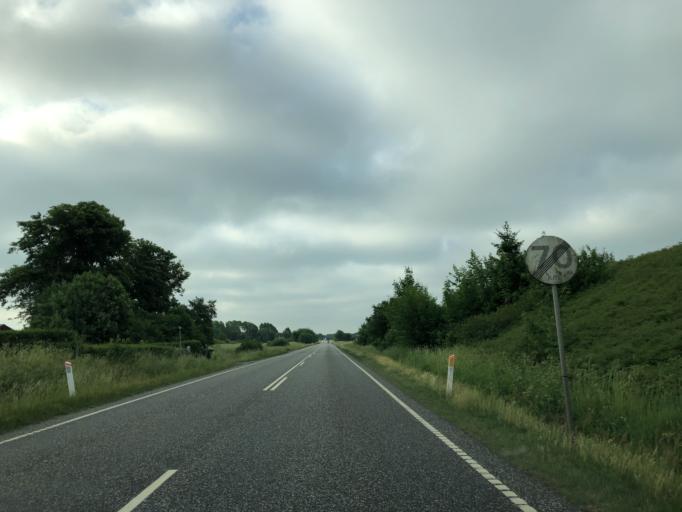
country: DK
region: South Denmark
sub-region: Vejle Kommune
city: Give
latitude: 55.8064
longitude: 9.2587
